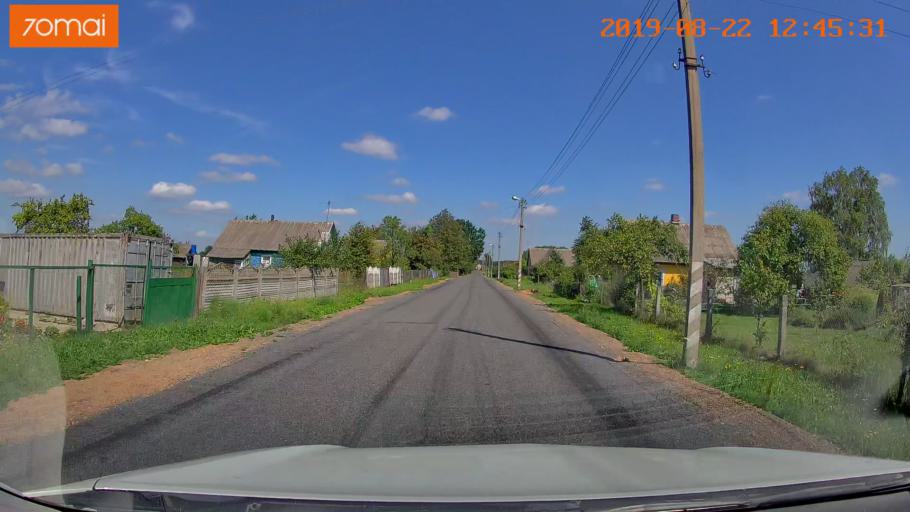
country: BY
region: Minsk
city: Prawdzinski
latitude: 53.4581
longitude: 27.6202
